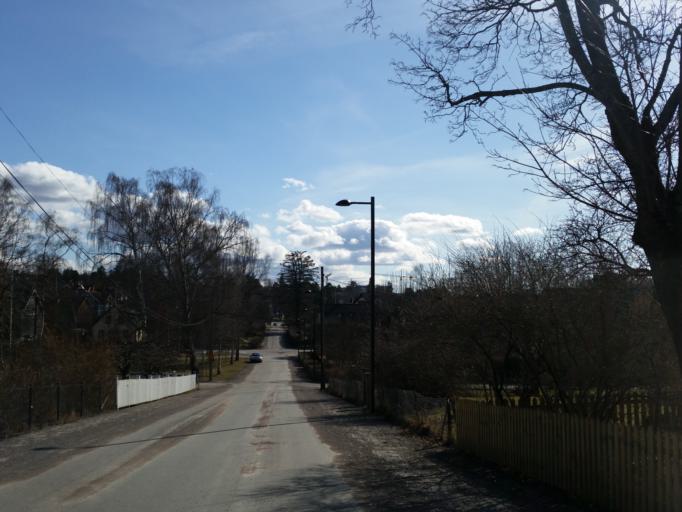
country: SE
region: Stockholm
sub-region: Sundbybergs Kommun
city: Sundbyberg
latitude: 59.3720
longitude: 17.9531
